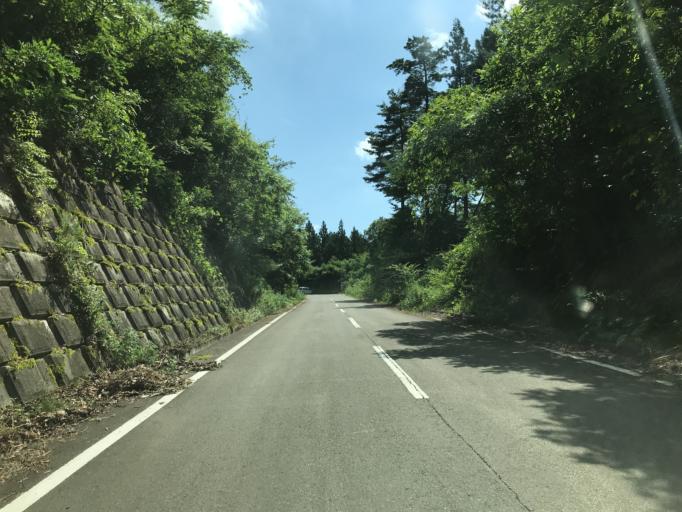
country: JP
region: Fukushima
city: Yanagawamachi-saiwaicho
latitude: 37.7758
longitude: 140.6703
